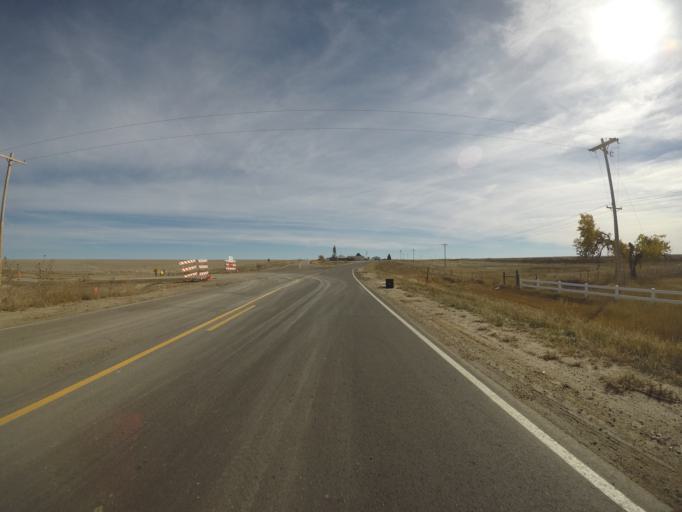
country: US
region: Colorado
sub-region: Adams County
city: Strasburg
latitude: 39.7385
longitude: -104.3030
